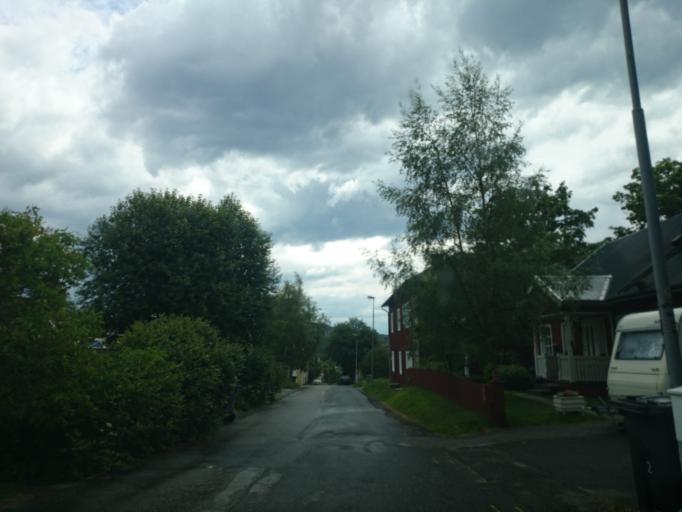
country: SE
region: Vaesternorrland
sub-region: Haernoesands Kommun
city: Haernoesand
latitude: 62.6260
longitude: 17.9235
